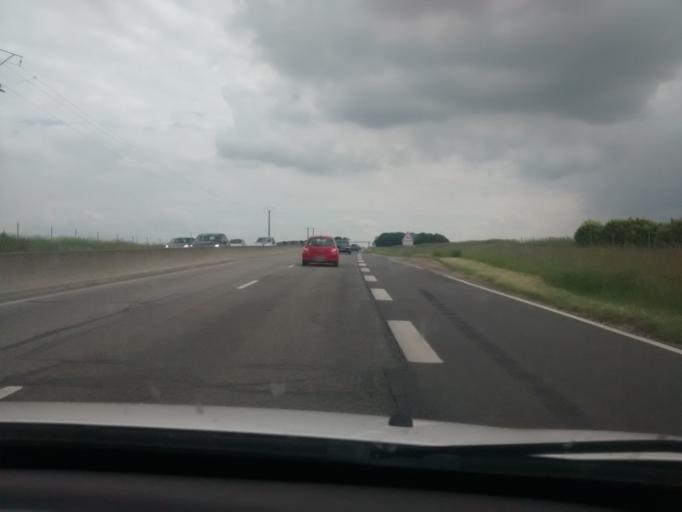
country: FR
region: Ile-de-France
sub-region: Departement des Yvelines
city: Rambouillet
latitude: 48.6181
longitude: 1.8312
